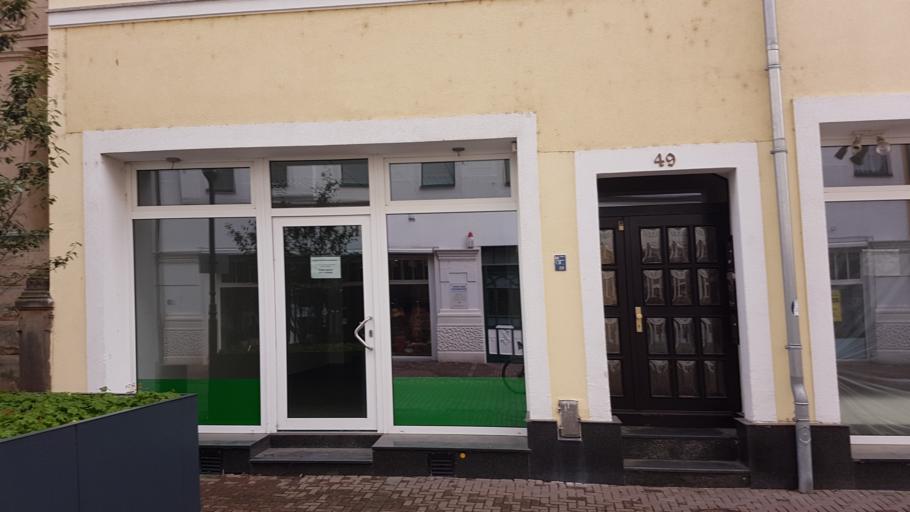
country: DE
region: Saxony
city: Riesa
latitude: 51.3036
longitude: 13.3073
